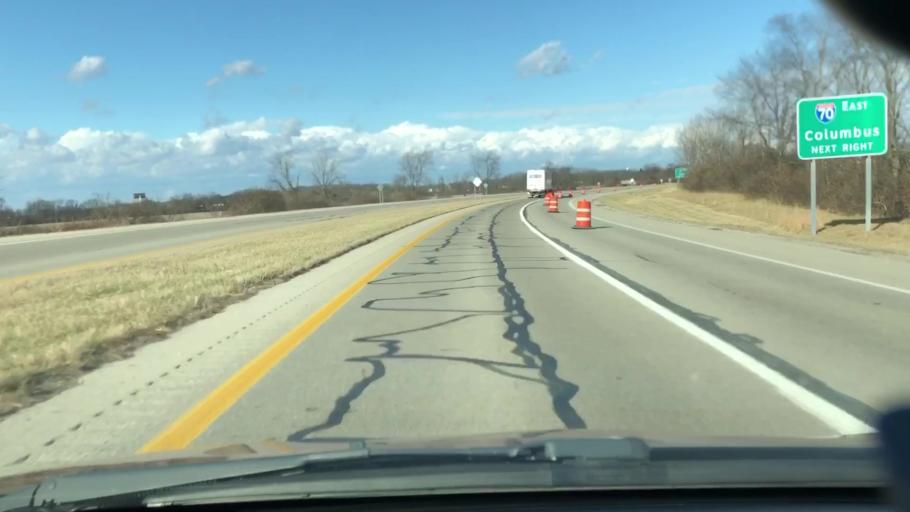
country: US
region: Ohio
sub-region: Clark County
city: Springfield
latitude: 39.8844
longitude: -83.8539
